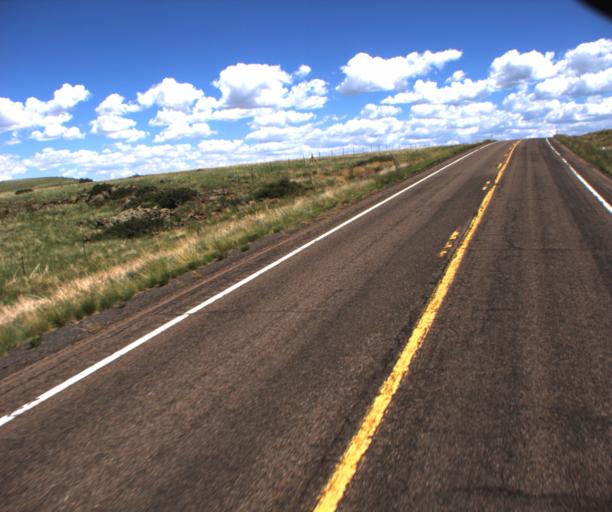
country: US
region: Arizona
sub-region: Apache County
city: Springerville
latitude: 34.2382
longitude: -109.5065
